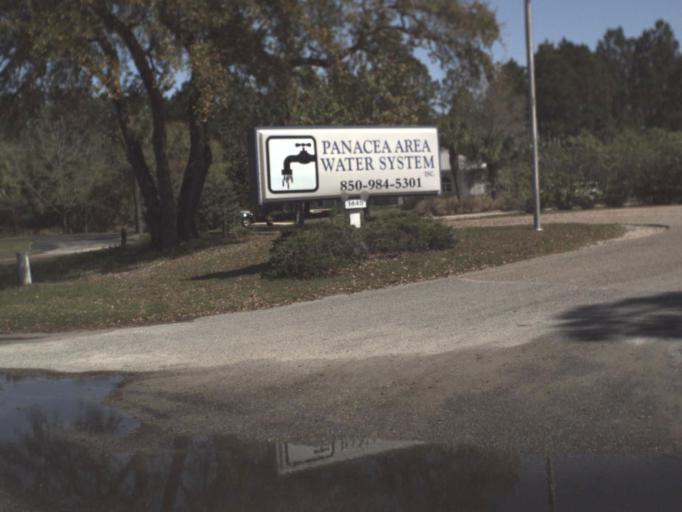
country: US
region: Florida
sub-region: Wakulla County
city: Crawfordville
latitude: 30.0326
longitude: -84.3903
